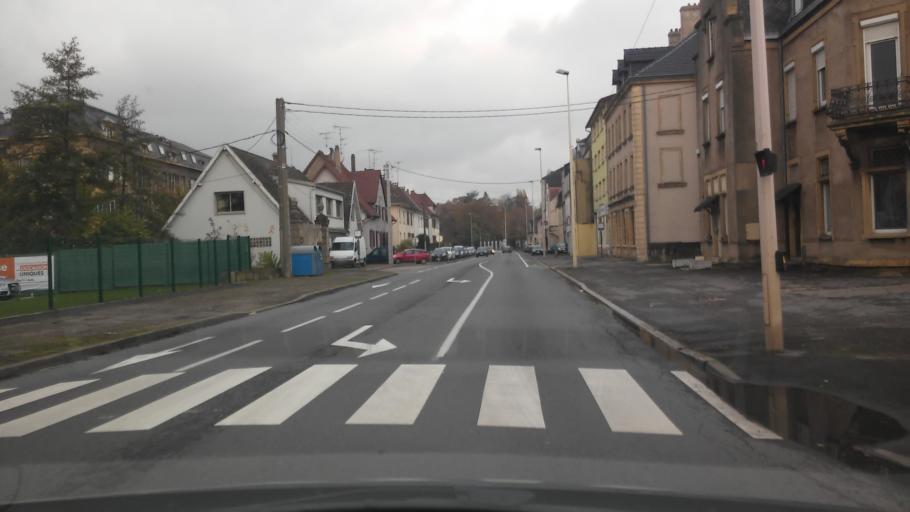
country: FR
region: Lorraine
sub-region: Departement de la Moselle
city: Terville
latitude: 49.3425
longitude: 6.1609
